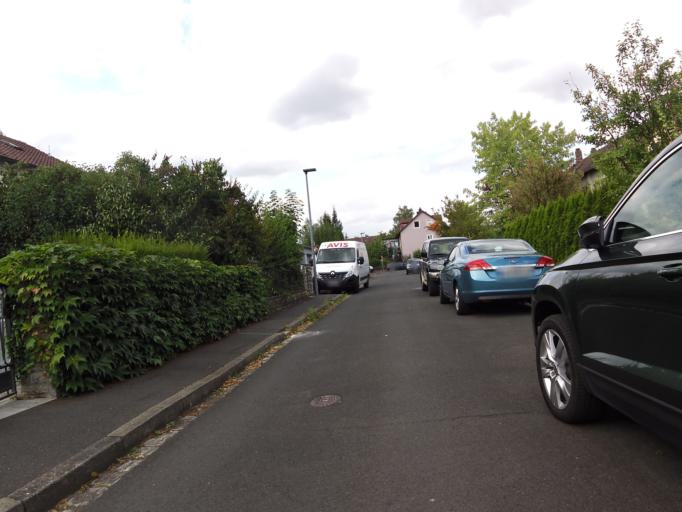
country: DE
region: Bavaria
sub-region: Regierungsbezirk Unterfranken
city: Veitshochheim
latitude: 49.8336
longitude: 9.8938
